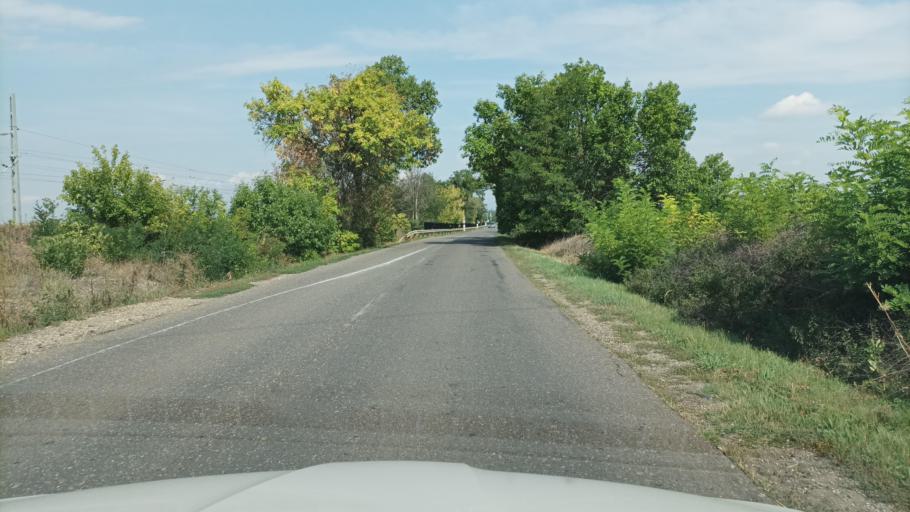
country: HU
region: Pest
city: Tura
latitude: 47.6353
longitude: 19.6344
